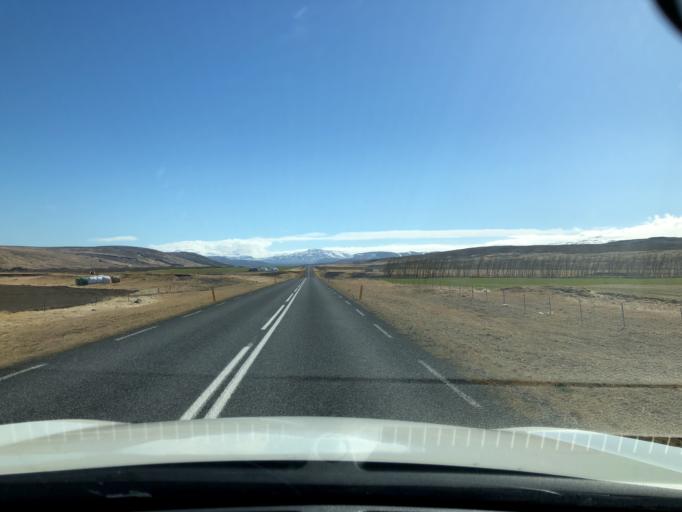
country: IS
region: South
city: Hveragerdi
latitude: 64.7015
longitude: -21.2061
